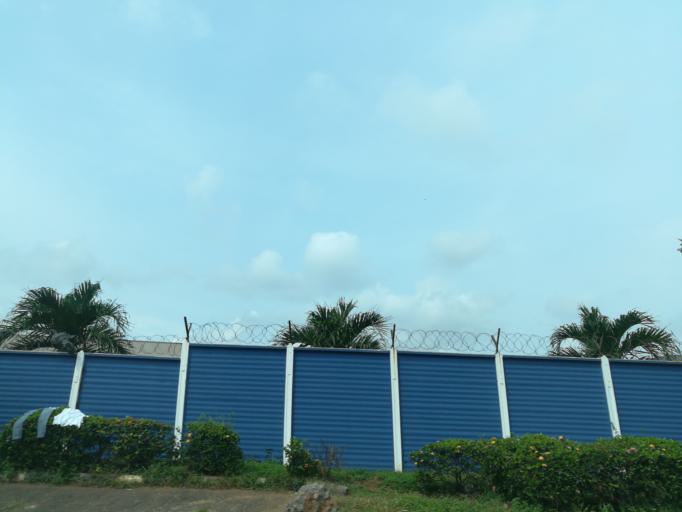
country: NG
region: Lagos
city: Ojota
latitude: 6.6052
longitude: 3.3711
